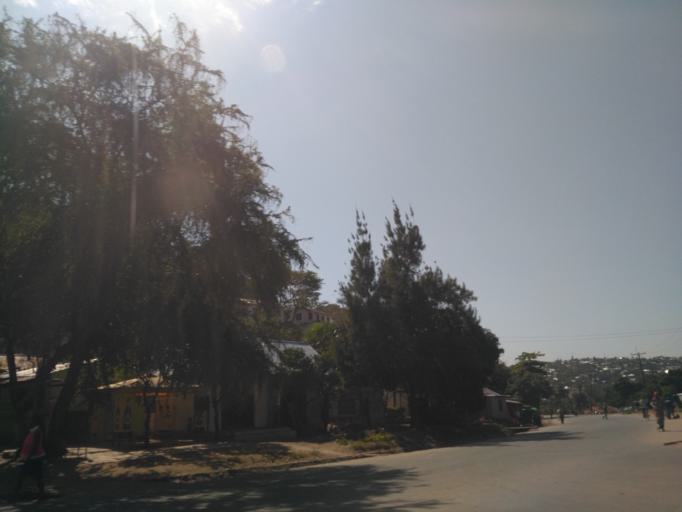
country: TZ
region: Mwanza
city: Mwanza
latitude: -2.4894
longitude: 32.8979
